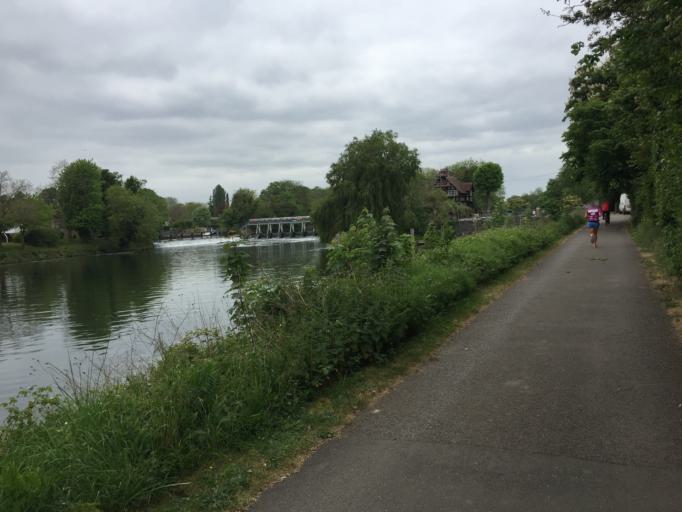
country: GB
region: England
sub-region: Royal Borough of Windsor and Maidenhead
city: Bray
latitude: 51.5090
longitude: -0.6886
